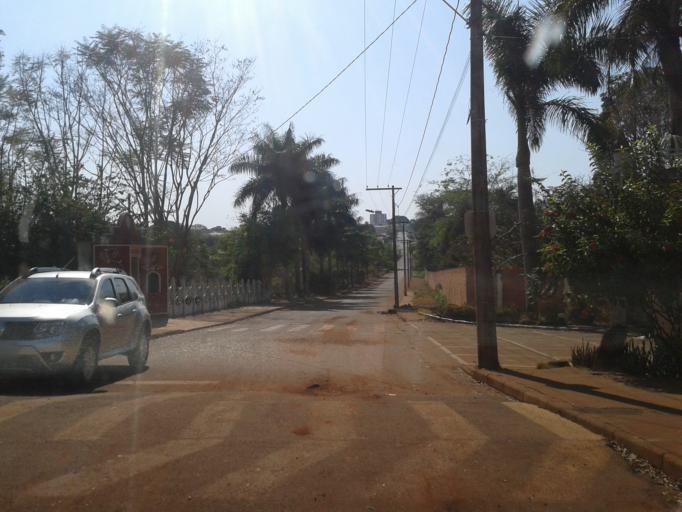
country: BR
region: Minas Gerais
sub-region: Ituiutaba
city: Ituiutaba
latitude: -18.9648
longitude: -49.4751
